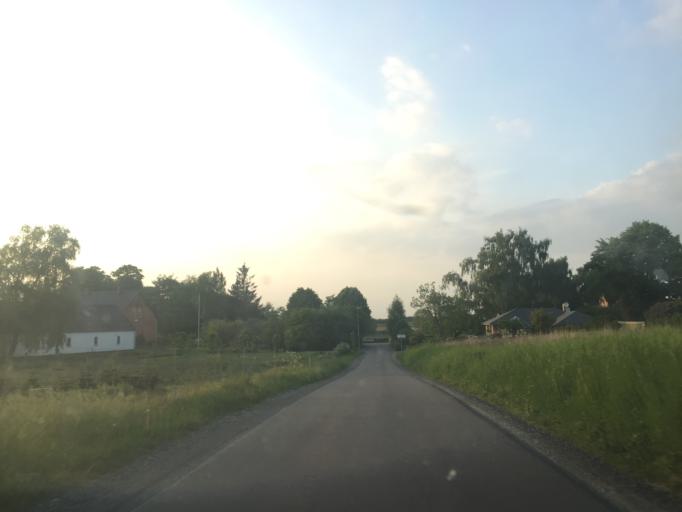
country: DK
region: South Denmark
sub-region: Odense Kommune
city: Bellinge
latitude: 55.3797
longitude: 10.3102
